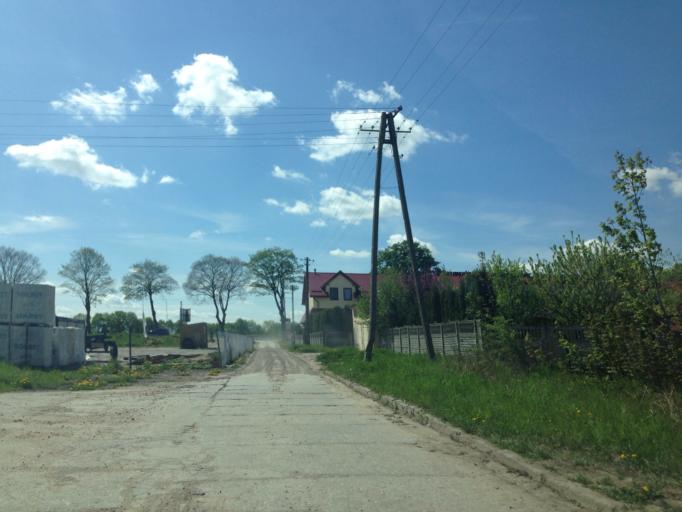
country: PL
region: Kujawsko-Pomorskie
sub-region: Powiat brodnicki
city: Brzozie
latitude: 53.3227
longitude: 19.5906
